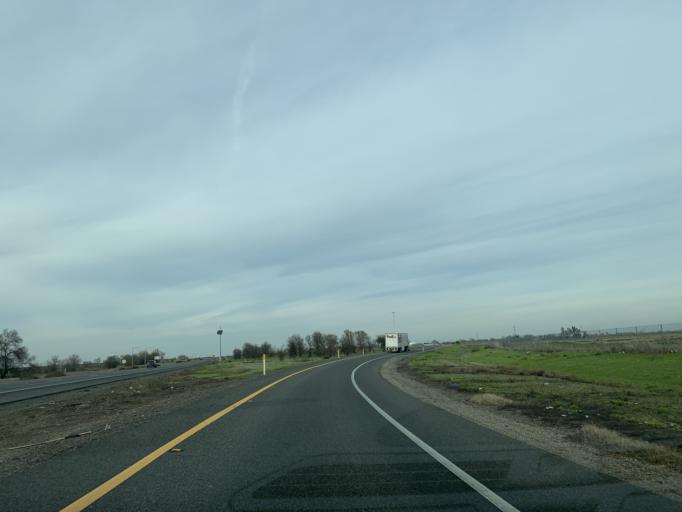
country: US
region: California
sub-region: Sacramento County
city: Elverta
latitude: 38.8146
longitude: -121.5435
